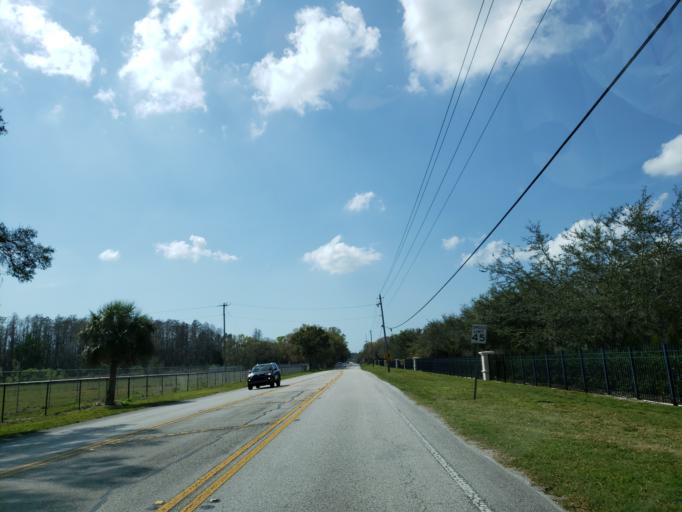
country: US
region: Florida
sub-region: Hillsborough County
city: Keystone
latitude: 28.1443
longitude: -82.6050
